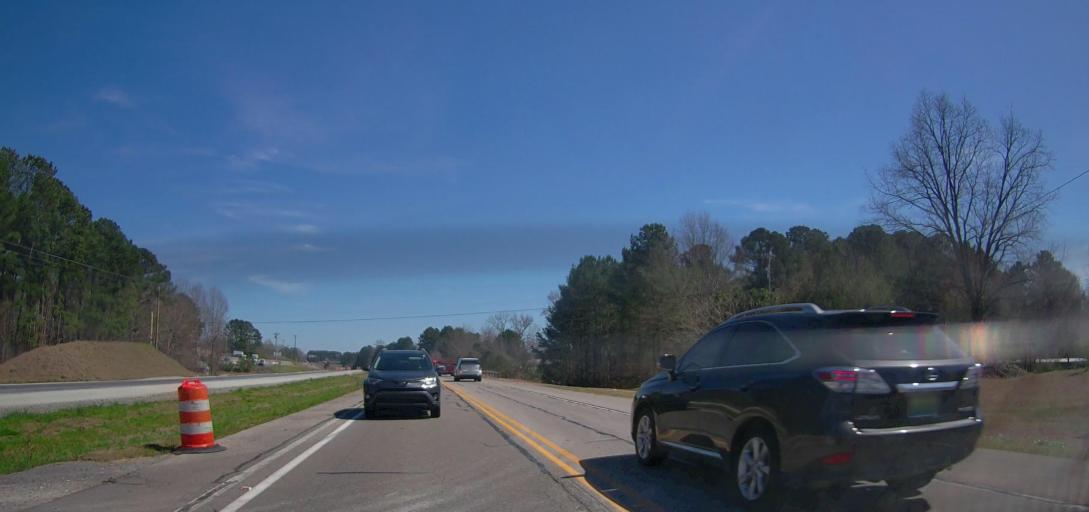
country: US
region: Alabama
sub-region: Cullman County
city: Cullman
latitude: 34.2005
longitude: -86.8206
